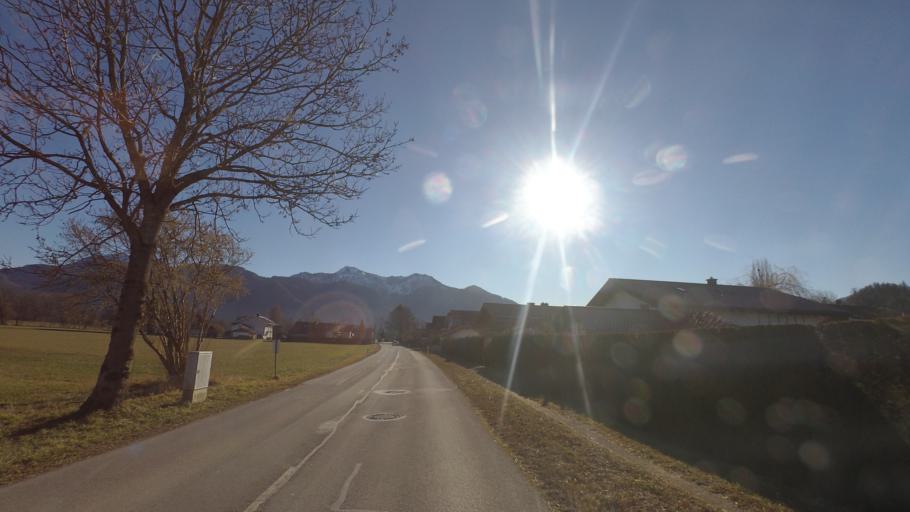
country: DE
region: Bavaria
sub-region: Upper Bavaria
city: Ubersee
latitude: 47.8102
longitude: 12.4806
